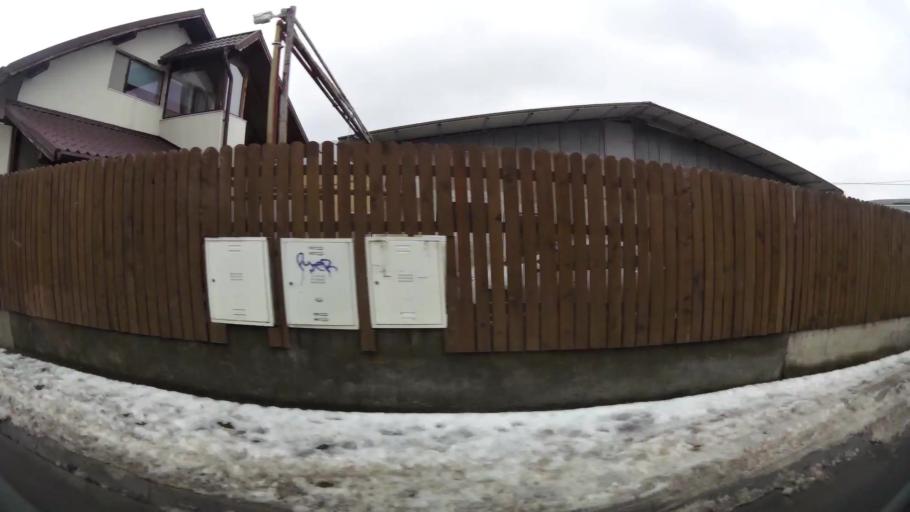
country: RO
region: Ilfov
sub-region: Comuna Otopeni
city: Otopeni
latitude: 44.5548
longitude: 26.0796
